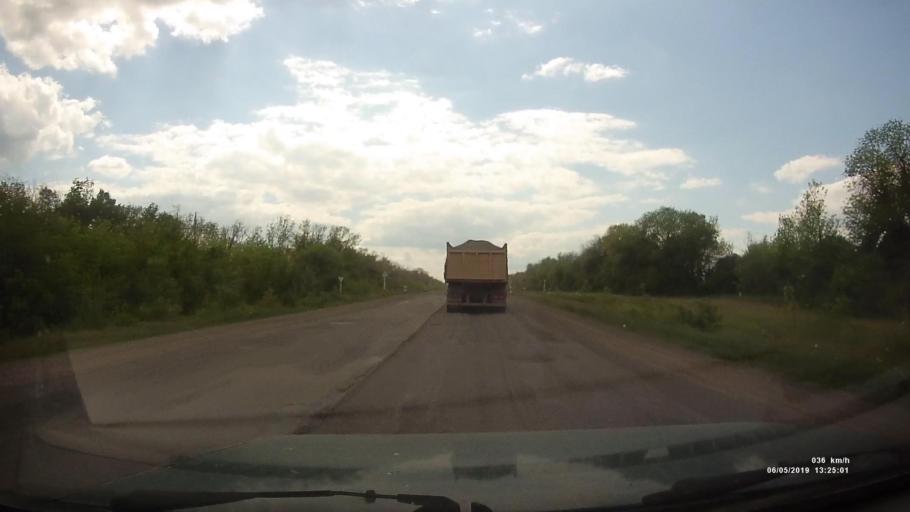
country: RU
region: Rostov
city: Ust'-Donetskiy
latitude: 47.6838
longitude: 40.9066
